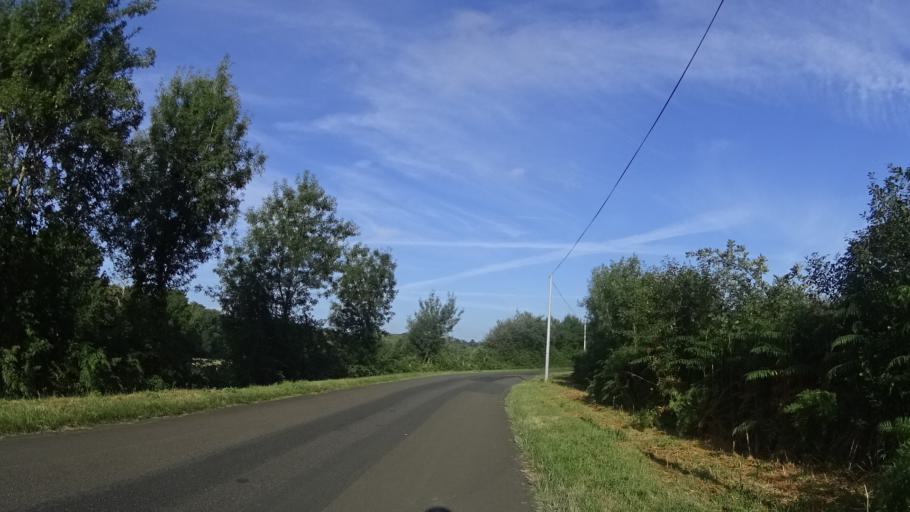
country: FR
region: Pays de la Loire
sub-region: Departement de la Sarthe
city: La Fleche
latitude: 47.6802
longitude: -0.1195
